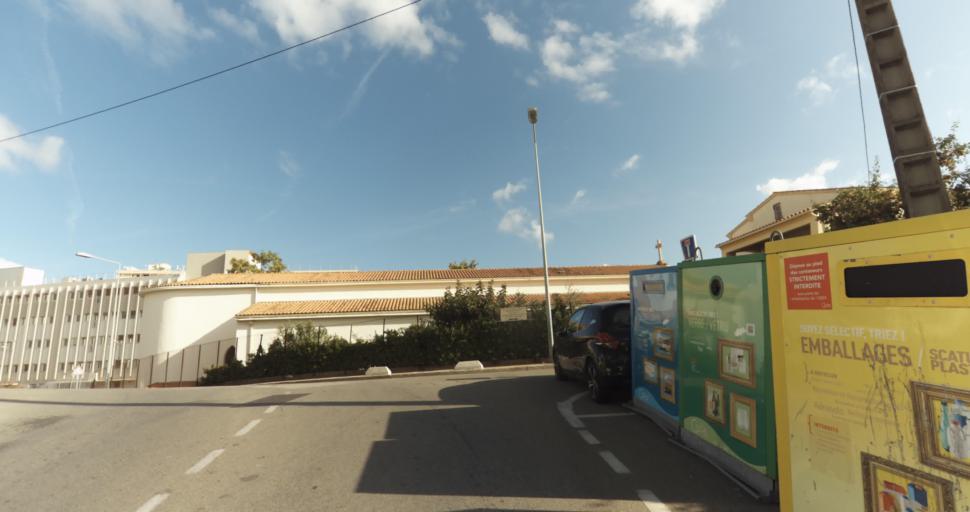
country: FR
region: Corsica
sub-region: Departement de la Corse-du-Sud
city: Ajaccio
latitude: 41.9279
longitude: 8.7353
